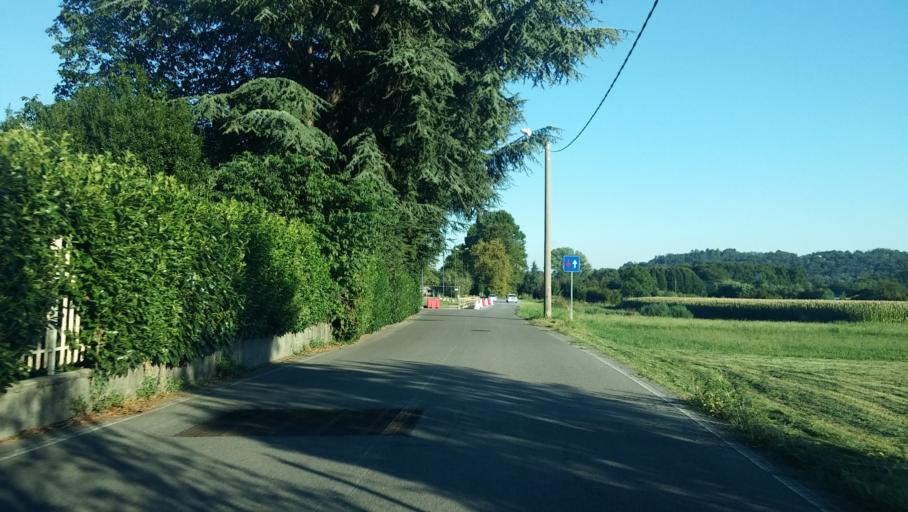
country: IT
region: Lombardy
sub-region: Provincia di Como
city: Erba
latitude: 45.8023
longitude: 9.2191
